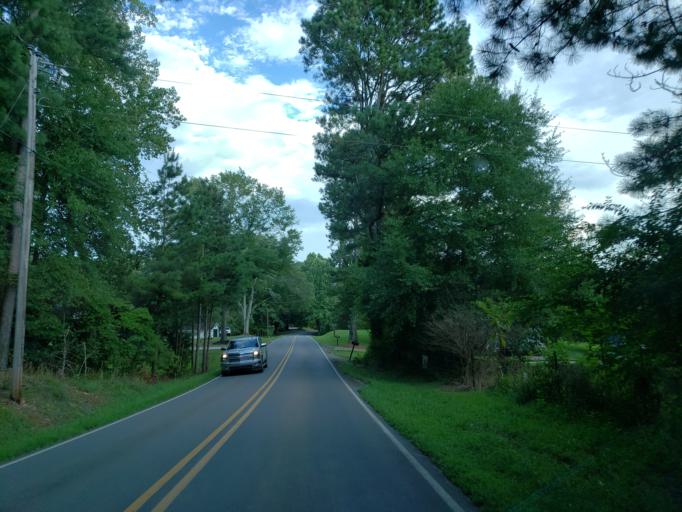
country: US
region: Georgia
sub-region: Cherokee County
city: Ball Ground
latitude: 34.3347
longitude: -84.4397
